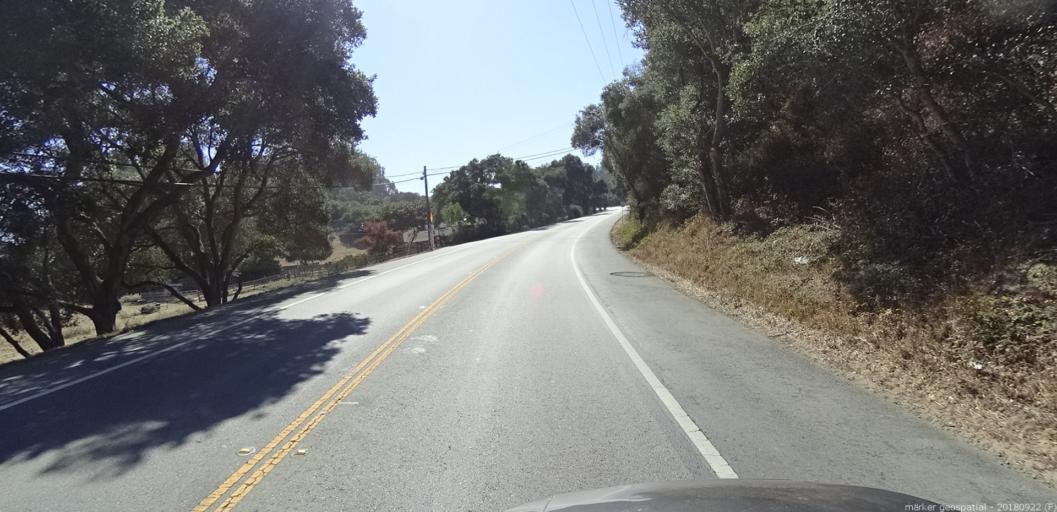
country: US
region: California
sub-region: Monterey County
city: Las Lomas
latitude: 36.8387
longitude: -121.6842
